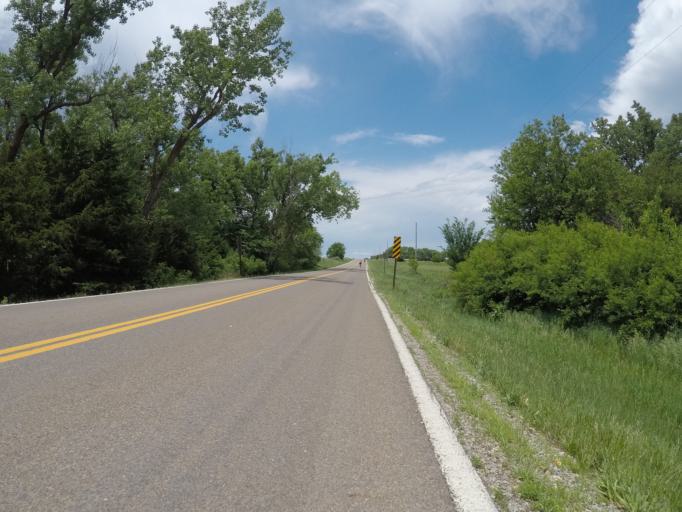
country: US
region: Kansas
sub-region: Morris County
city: Council Grove
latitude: 38.8545
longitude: -96.4300
